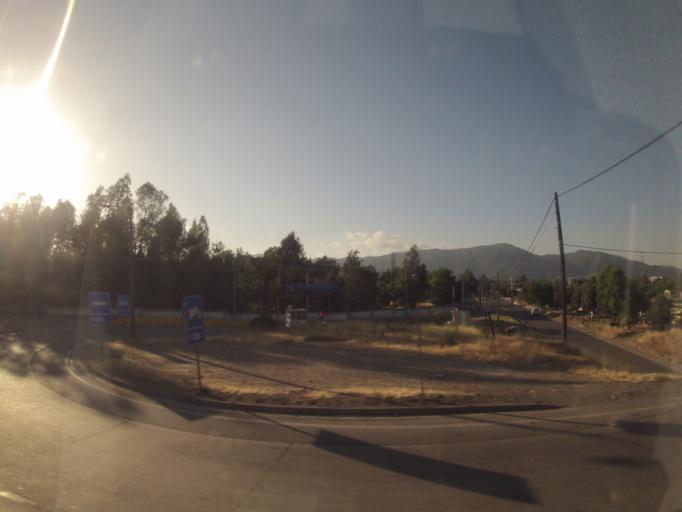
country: CL
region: O'Higgins
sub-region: Provincia de Colchagua
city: Chimbarongo
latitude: -34.5942
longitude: -70.9726
